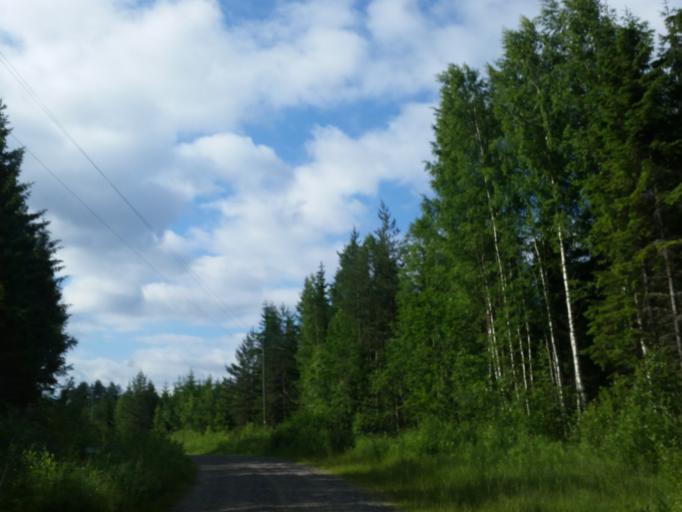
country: FI
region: Northern Savo
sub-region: Sisae-Savo
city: Tervo
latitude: 63.0635
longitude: 26.6110
